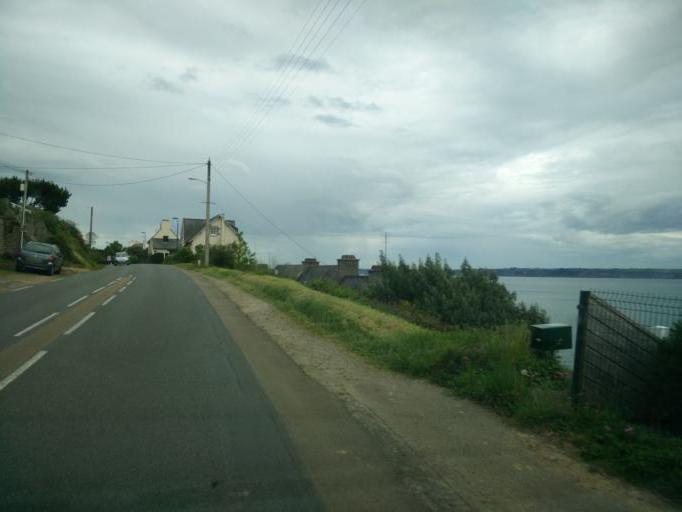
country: FR
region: Brittany
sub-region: Departement du Finistere
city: Locquirec
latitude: 48.6824
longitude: -3.6556
